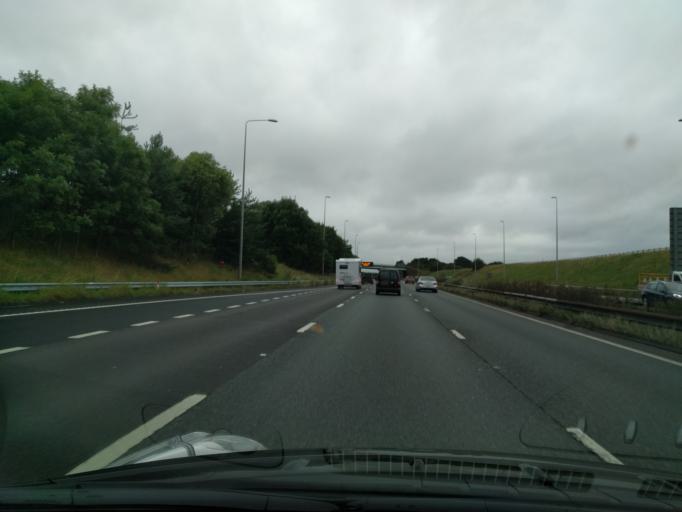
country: GB
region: England
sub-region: St. Helens
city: Newton-le-Willows
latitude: 53.4431
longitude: -2.5878
